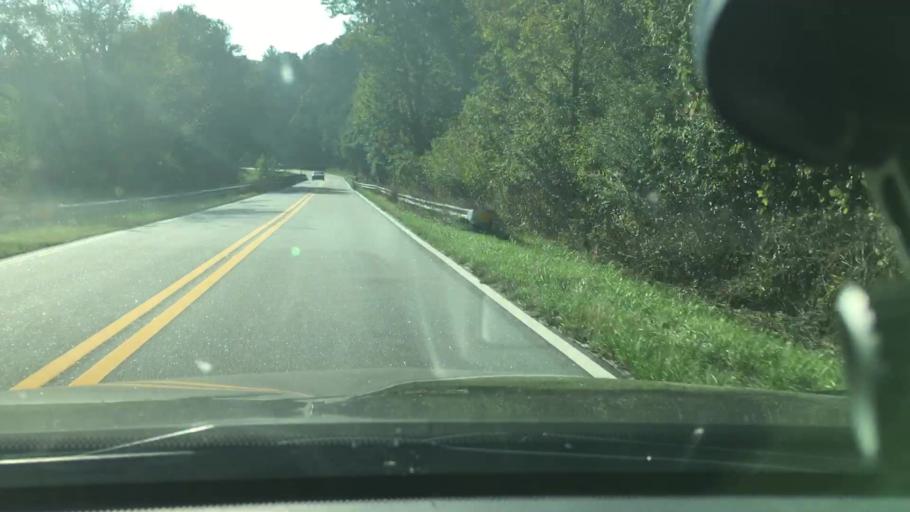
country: US
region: North Carolina
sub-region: Rutherford County
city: Rutherfordton
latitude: 35.3267
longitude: -82.0719
